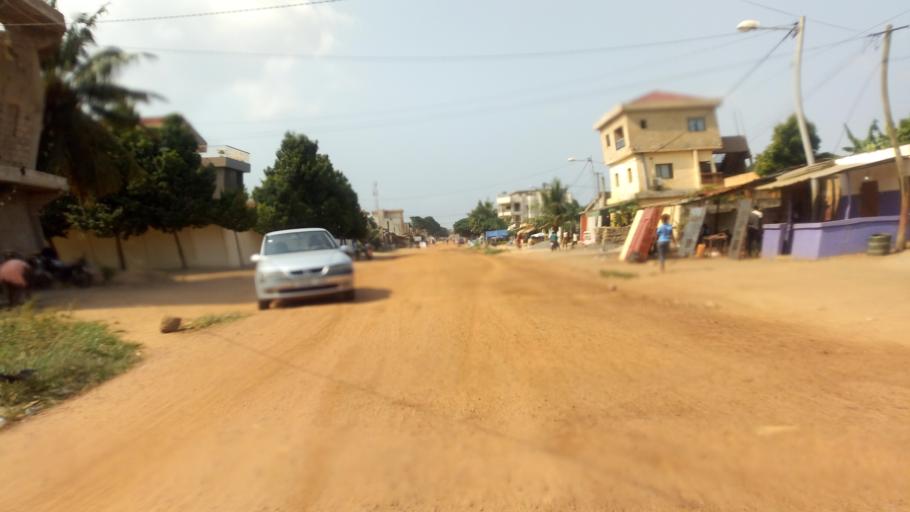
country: TG
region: Maritime
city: Lome
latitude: 6.1936
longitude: 1.1810
